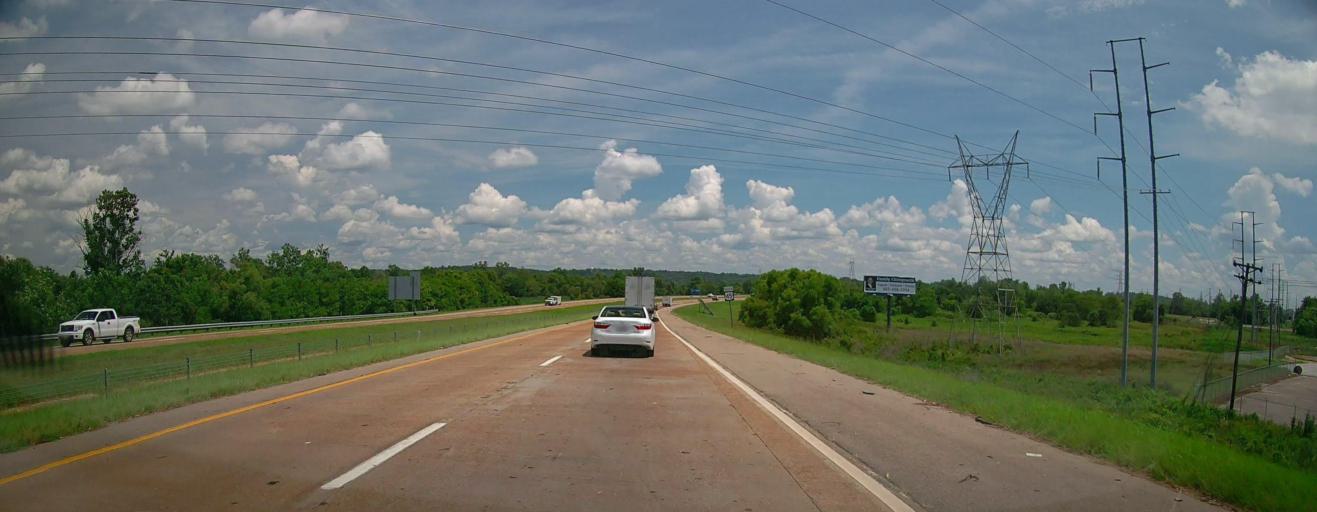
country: US
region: Mississippi
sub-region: Lee County
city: Tupelo
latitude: 34.2698
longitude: -88.6984
